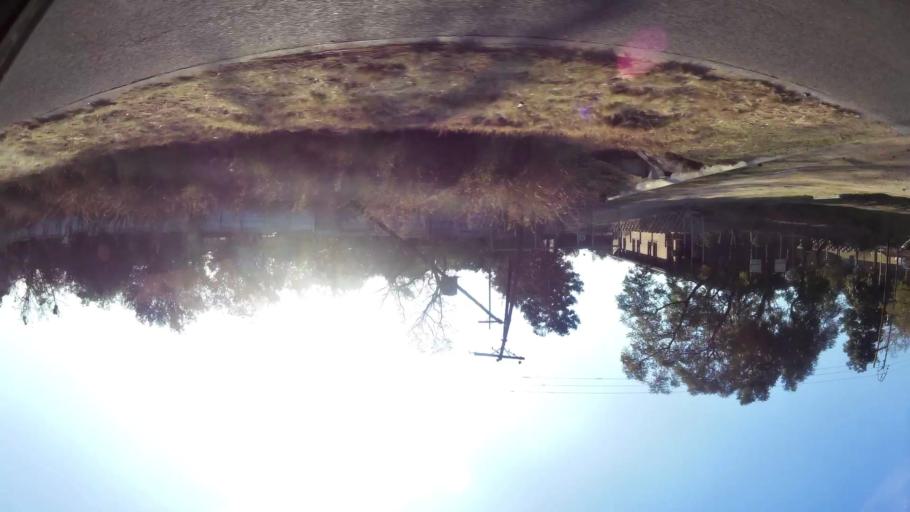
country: ZA
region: Gauteng
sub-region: West Rand District Municipality
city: Muldersdriseloop
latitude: -26.0499
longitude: 27.9059
